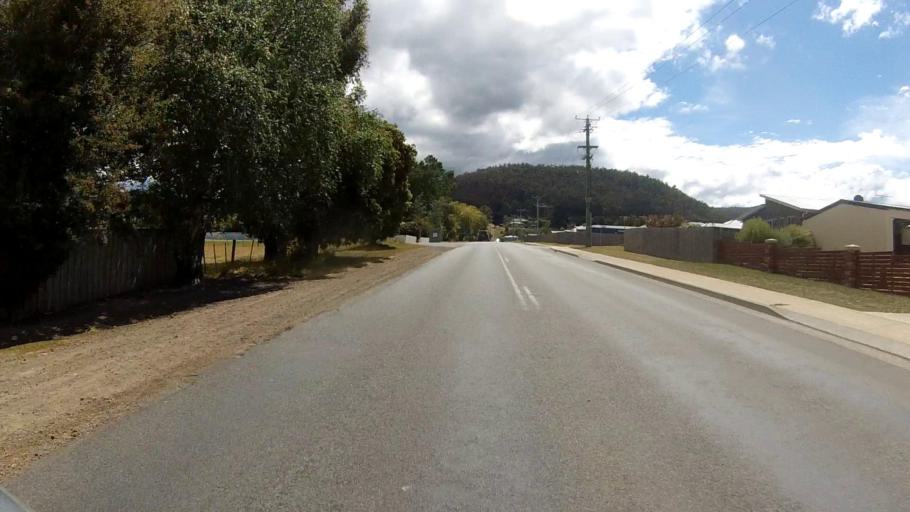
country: AU
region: Tasmania
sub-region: Huon Valley
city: Huonville
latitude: -43.0119
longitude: 147.0388
